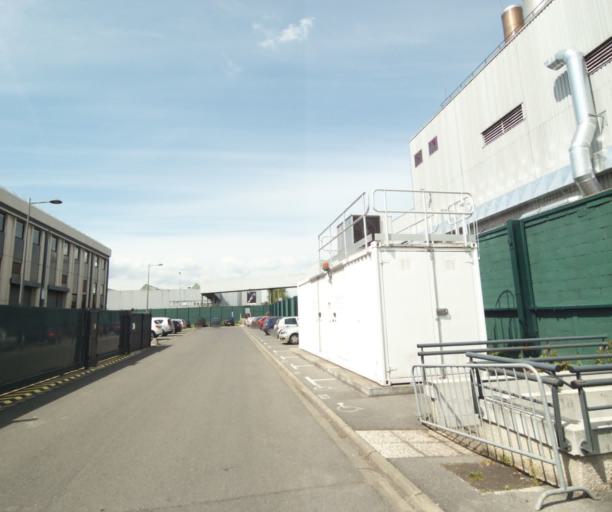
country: FR
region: Ile-de-France
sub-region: Departement du Val-d'Oise
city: Argenteuil
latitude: 48.9356
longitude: 2.2531
